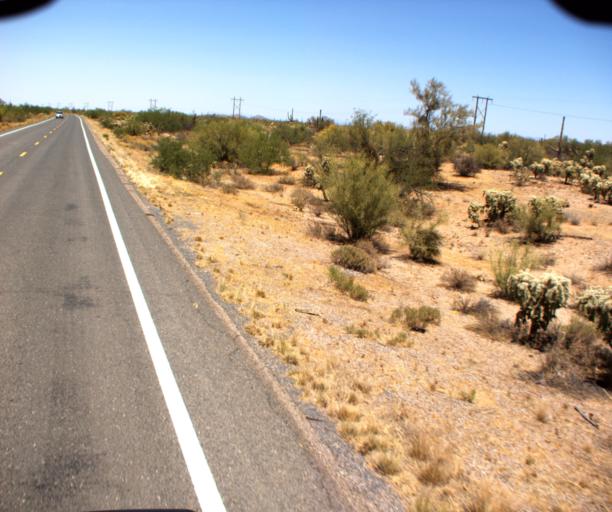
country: US
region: Arizona
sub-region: Pinal County
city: Florence
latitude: 32.7890
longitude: -111.1725
